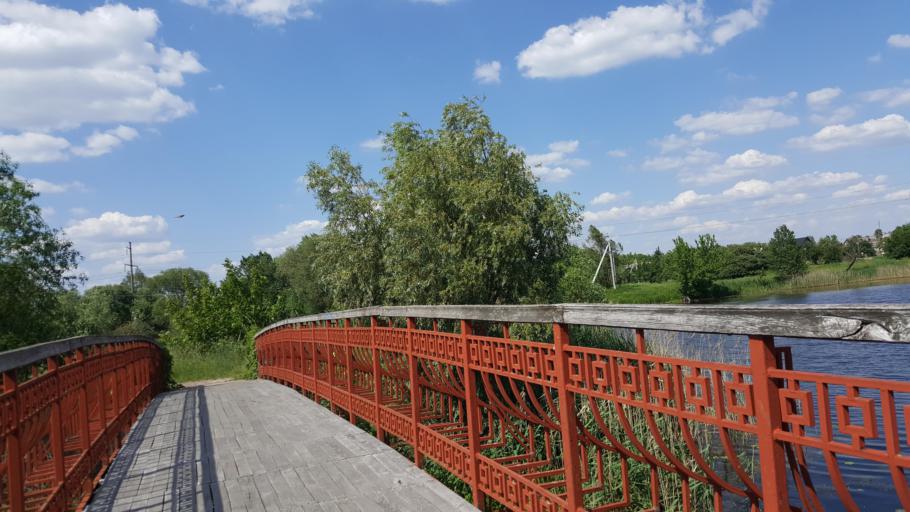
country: BY
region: Brest
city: Kobryn
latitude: 52.2158
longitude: 24.3538
